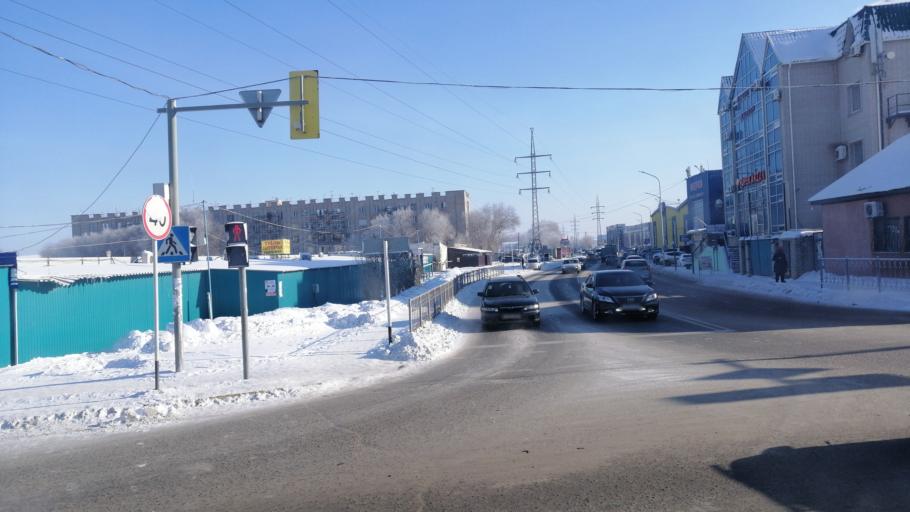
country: KZ
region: Aqtoebe
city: Aqtobe
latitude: 50.2958
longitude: 57.1982
